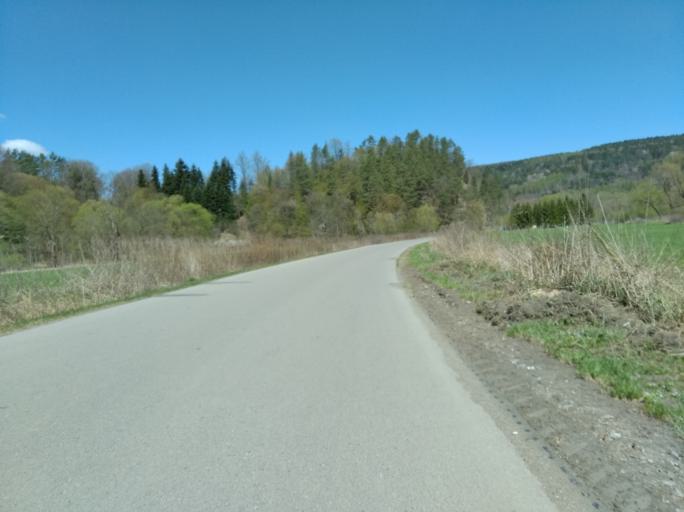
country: PL
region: Subcarpathian Voivodeship
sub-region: Powiat brzozowski
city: Dydnia
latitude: 49.6887
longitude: 22.2368
